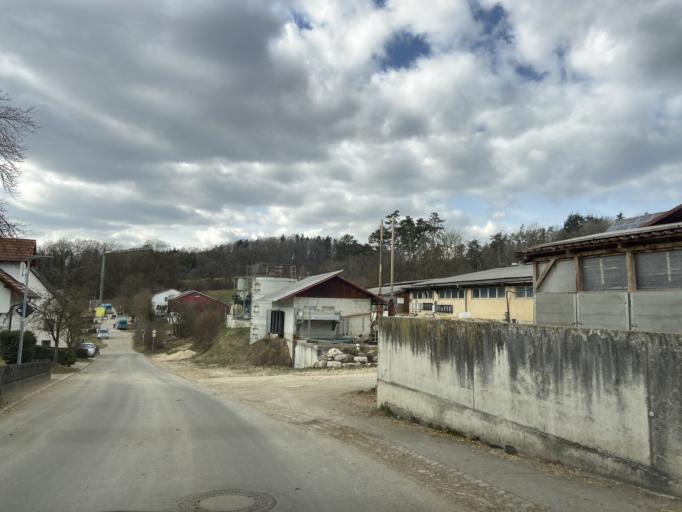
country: DE
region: Baden-Wuerttemberg
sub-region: Tuebingen Region
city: Bingen
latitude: 48.1127
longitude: 9.2567
